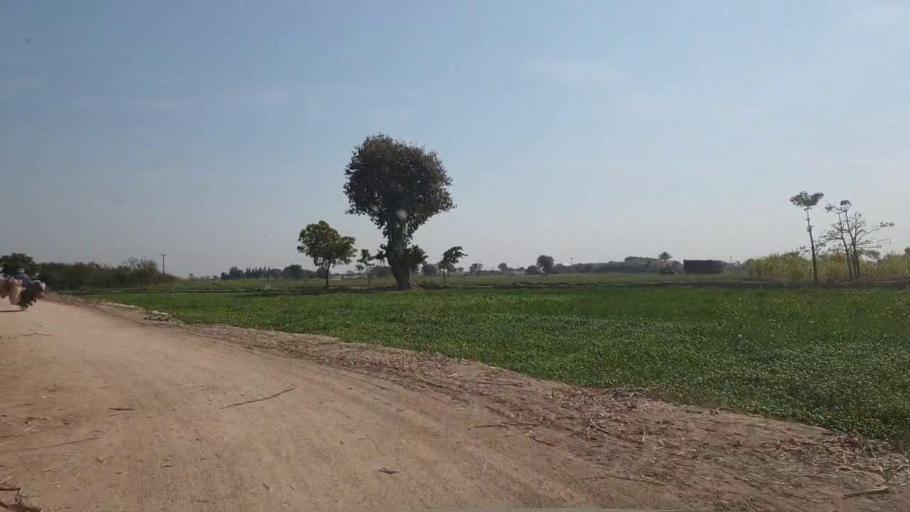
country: PK
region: Sindh
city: Chambar
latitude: 25.3457
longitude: 68.8355
